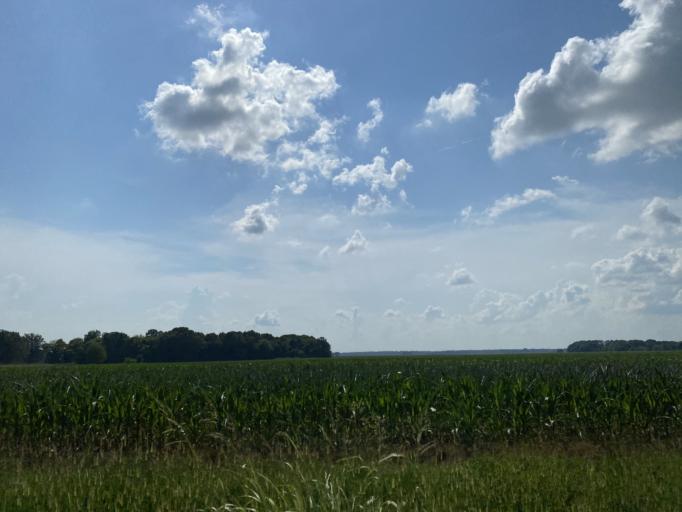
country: US
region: Alabama
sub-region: Lawrence County
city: Town Creek
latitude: 34.6687
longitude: -87.4060
